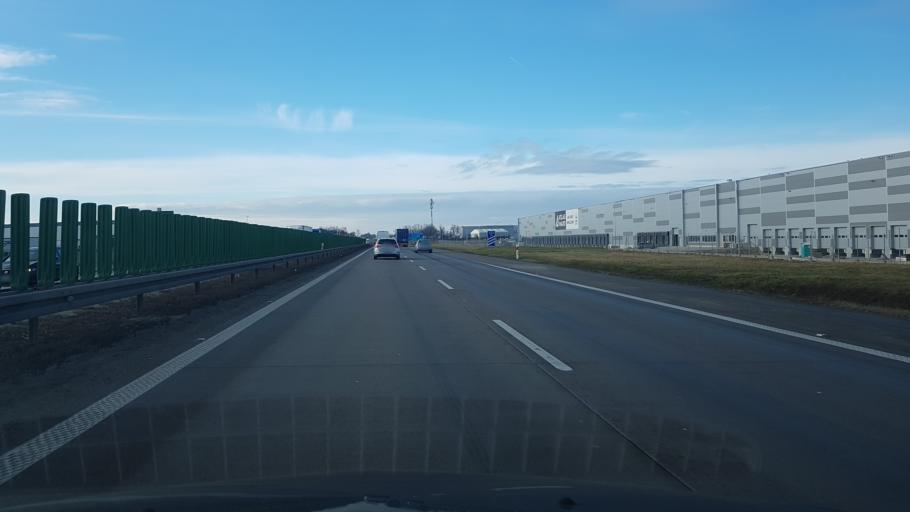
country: PL
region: Lower Silesian Voivodeship
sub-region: Powiat wroclawski
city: Tyniec Maly
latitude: 51.0398
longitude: 16.9041
